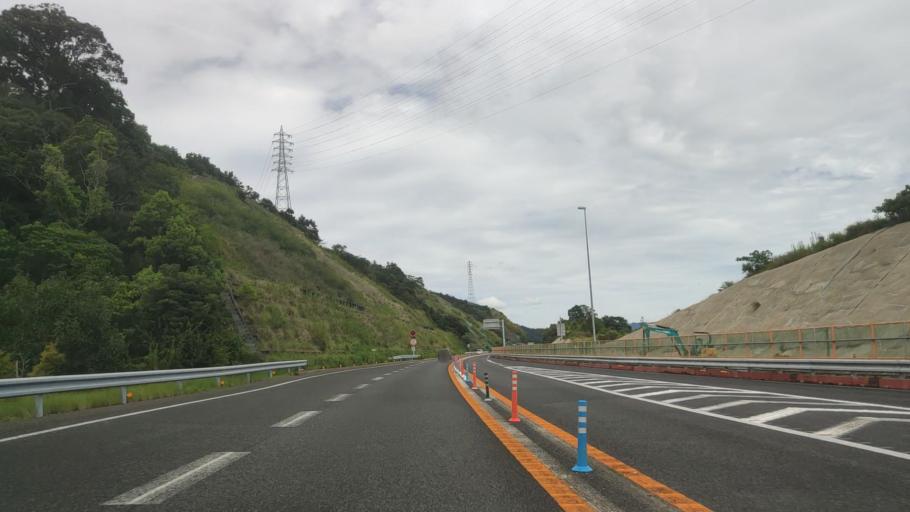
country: JP
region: Wakayama
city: Gobo
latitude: 33.8282
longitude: 135.2193
